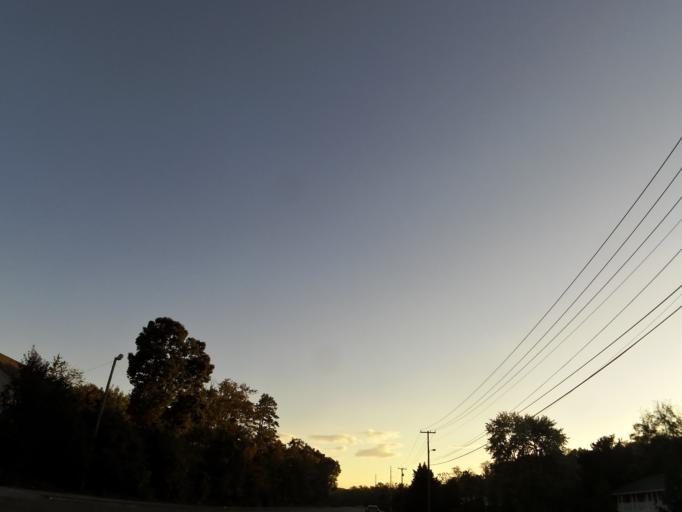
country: US
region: Tennessee
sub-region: Knox County
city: Farragut
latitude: 35.9373
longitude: -84.0602
